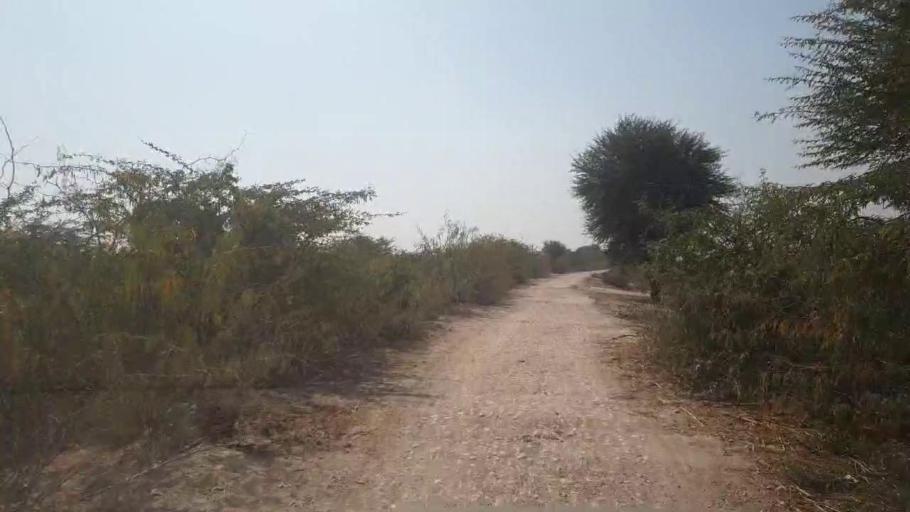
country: PK
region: Sindh
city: Chambar
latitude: 25.2396
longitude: 68.8267
